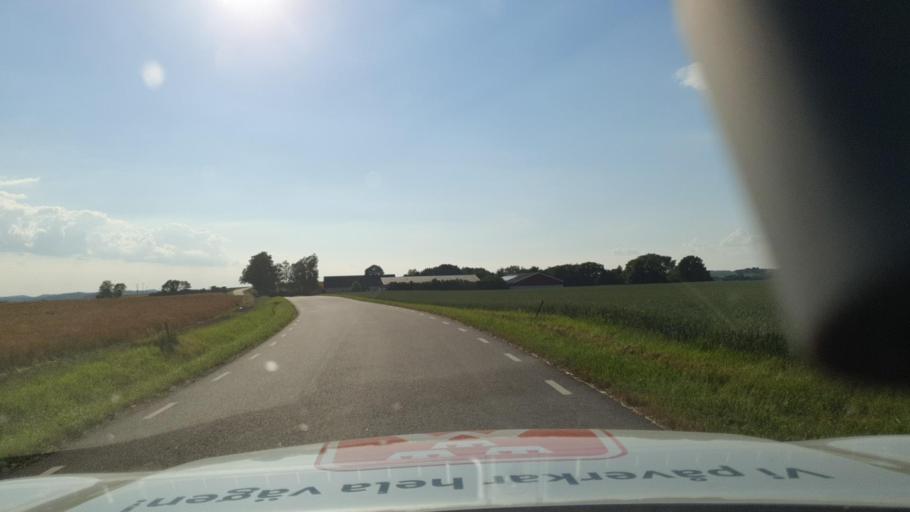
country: SE
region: Skane
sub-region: Skurups Kommun
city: Rydsgard
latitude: 55.5058
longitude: 13.5672
